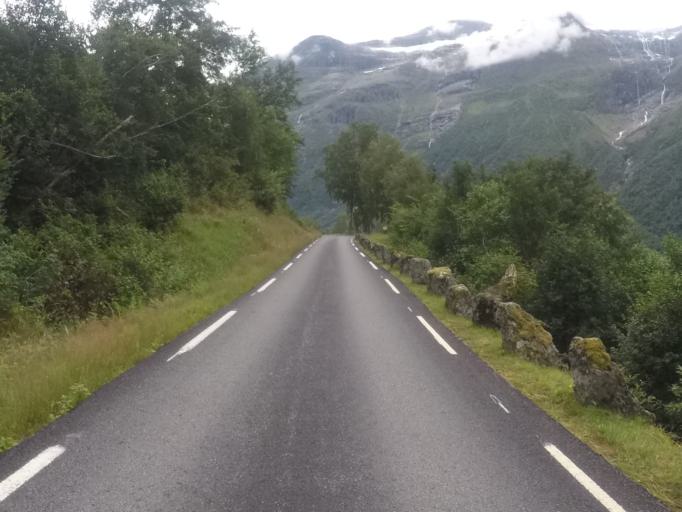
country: NO
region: Sogn og Fjordane
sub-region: Stryn
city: Stryn
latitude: 61.8354
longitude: 6.9490
